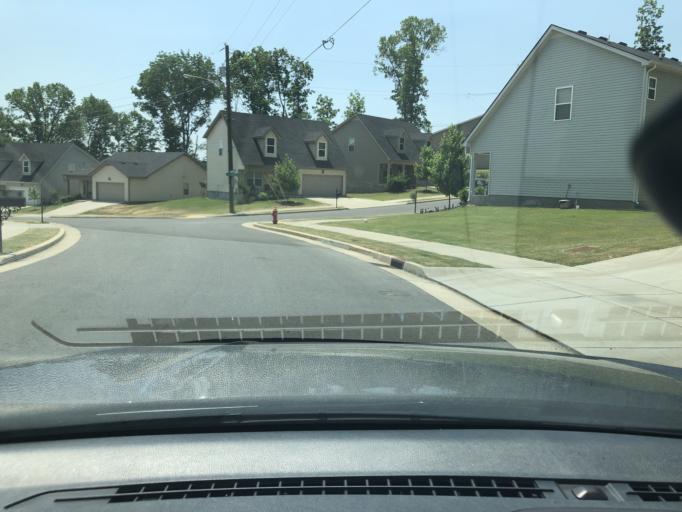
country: US
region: Tennessee
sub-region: Rutherford County
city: La Vergne
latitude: 36.0565
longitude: -86.6136
